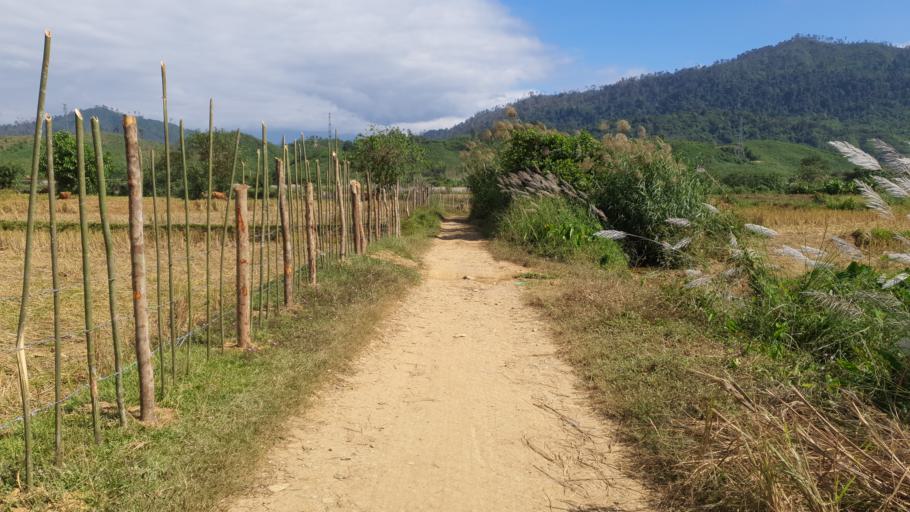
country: LA
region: Bolikhamxai
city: Bolikhan
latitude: 18.9064
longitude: 103.7422
